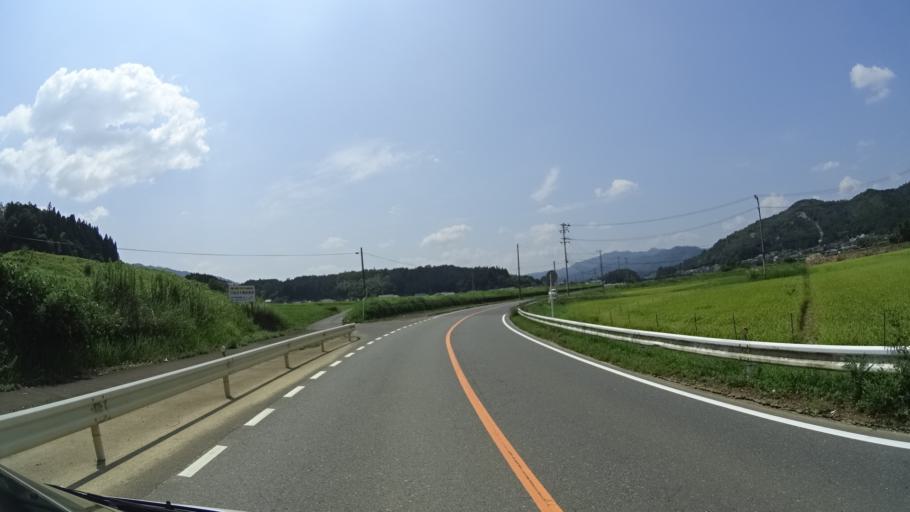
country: JP
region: Kyoto
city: Fukuchiyama
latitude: 35.2521
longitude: 135.1729
